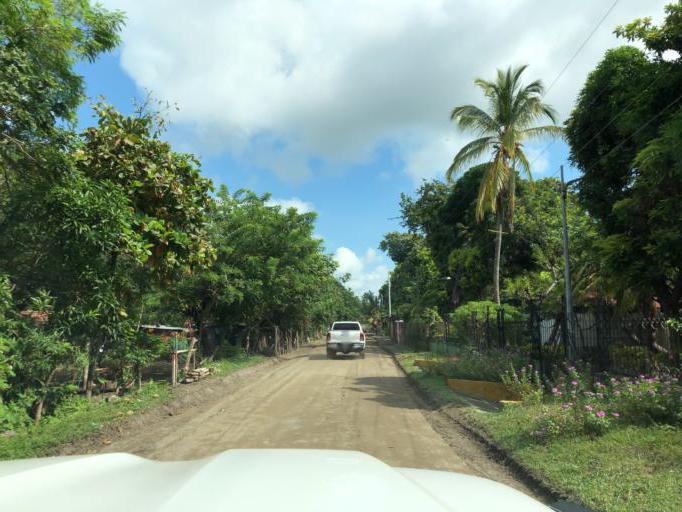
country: NI
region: Granada
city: Granada
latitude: 11.9911
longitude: -85.9382
